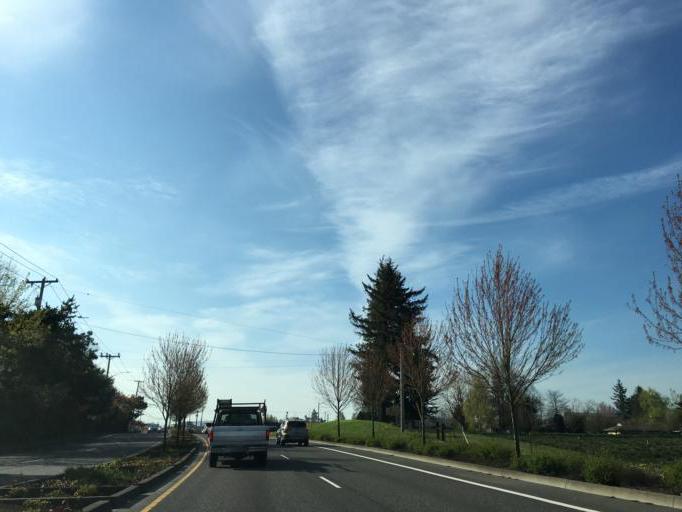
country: US
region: Oregon
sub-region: Multnomah County
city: Wood Village
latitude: 45.5219
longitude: -122.4132
